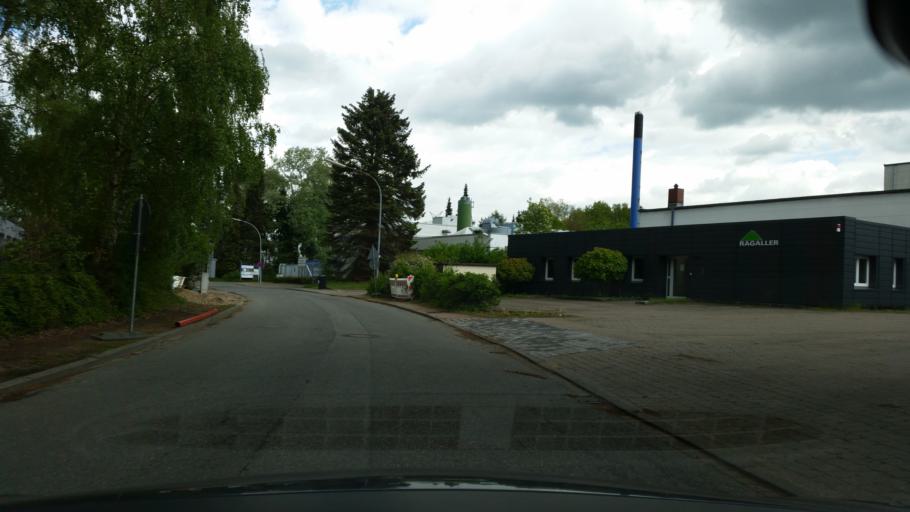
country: DE
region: Hamburg
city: Langenhorn
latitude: 53.7088
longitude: 10.0253
